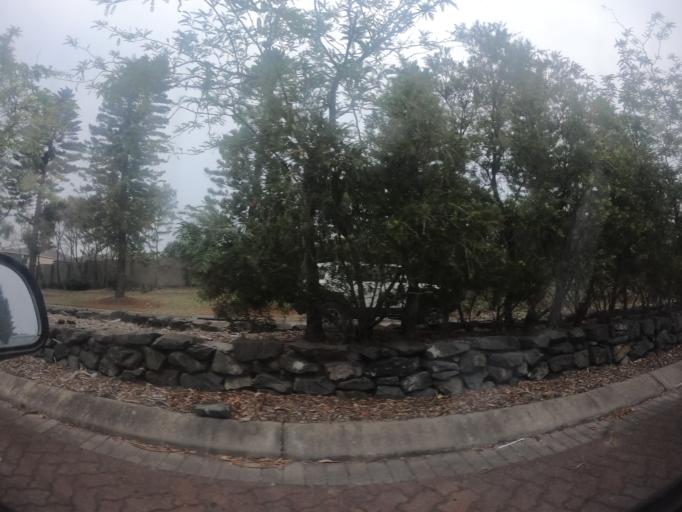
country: AU
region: New South Wales
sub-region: Shellharbour
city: Flinders
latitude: -34.5889
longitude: 150.8553
